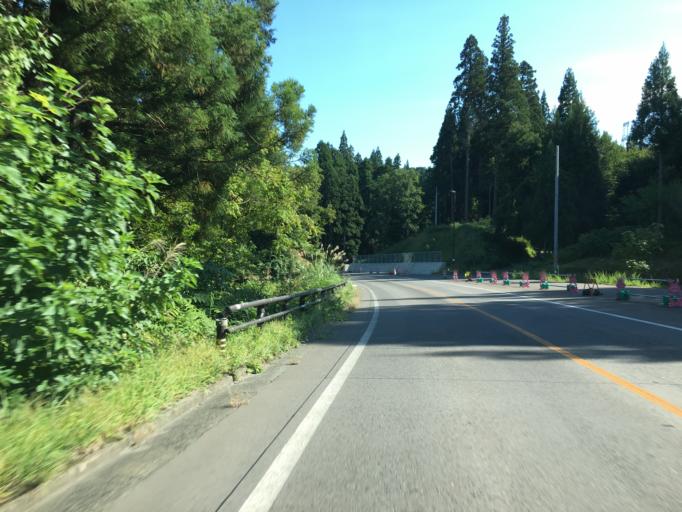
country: JP
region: Fukushima
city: Kitakata
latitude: 37.6524
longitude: 139.5869
